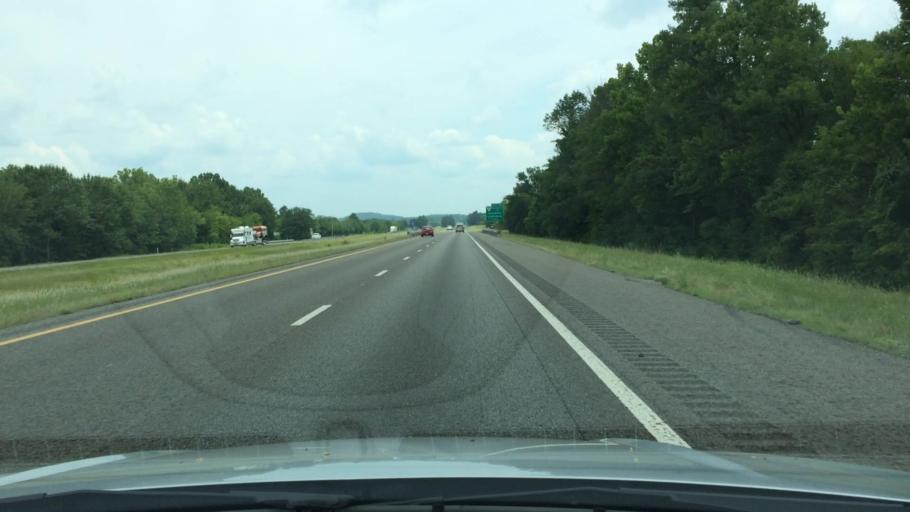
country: US
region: Tennessee
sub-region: Marshall County
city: Cornersville
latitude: 35.4314
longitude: -86.8798
